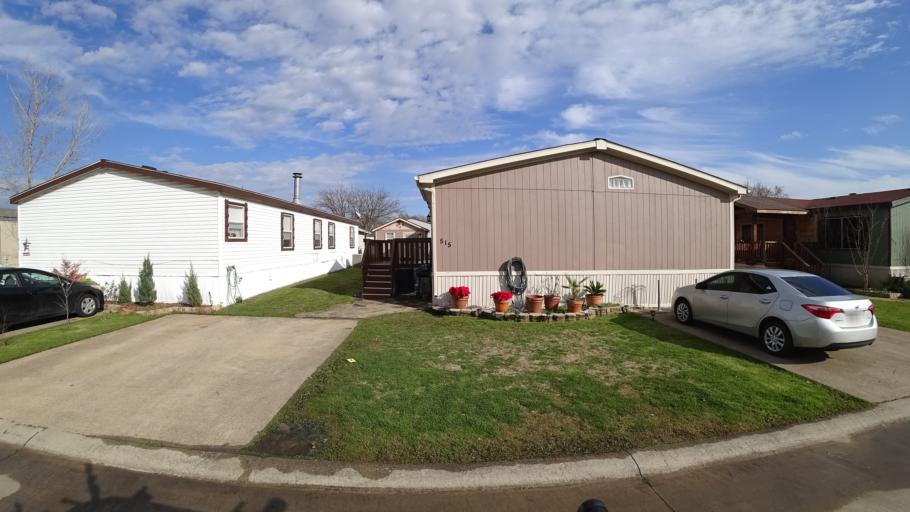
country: US
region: Texas
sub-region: Dallas County
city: Coppell
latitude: 32.9953
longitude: -97.0180
